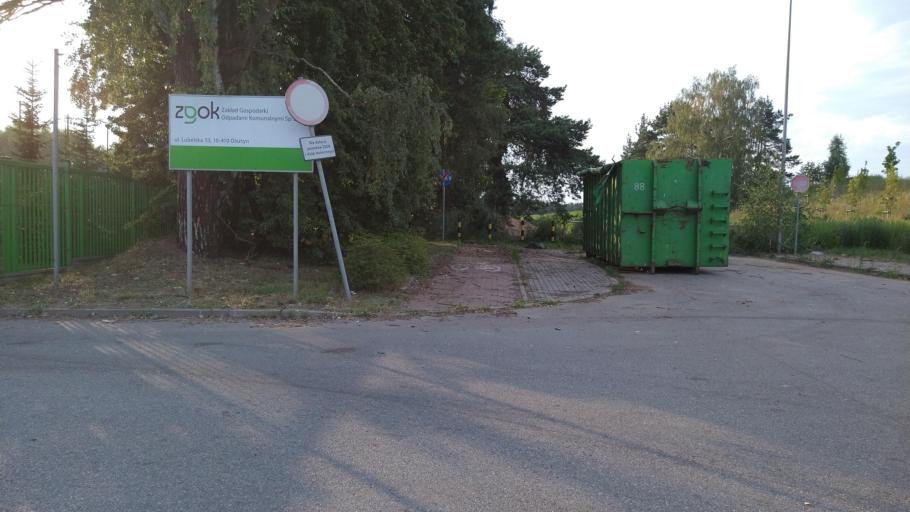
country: PL
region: Warmian-Masurian Voivodeship
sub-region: Powiat olsztynski
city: Olsztyn
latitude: 53.7888
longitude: 20.5529
